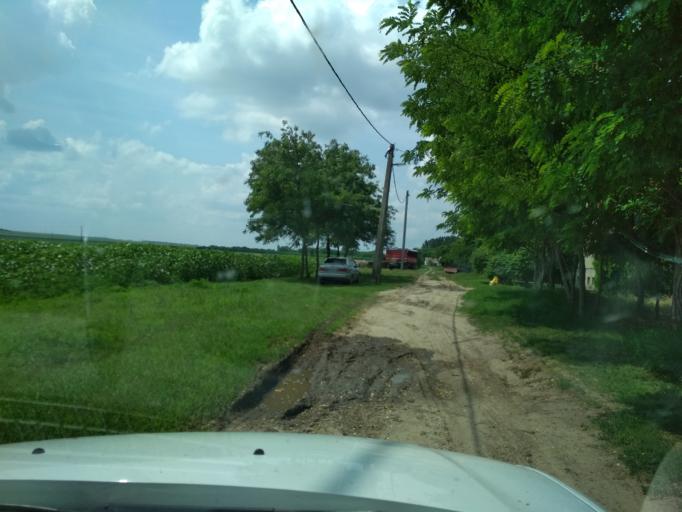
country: HU
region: Pest
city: Tapioszentmarton
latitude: 47.3422
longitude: 19.7313
